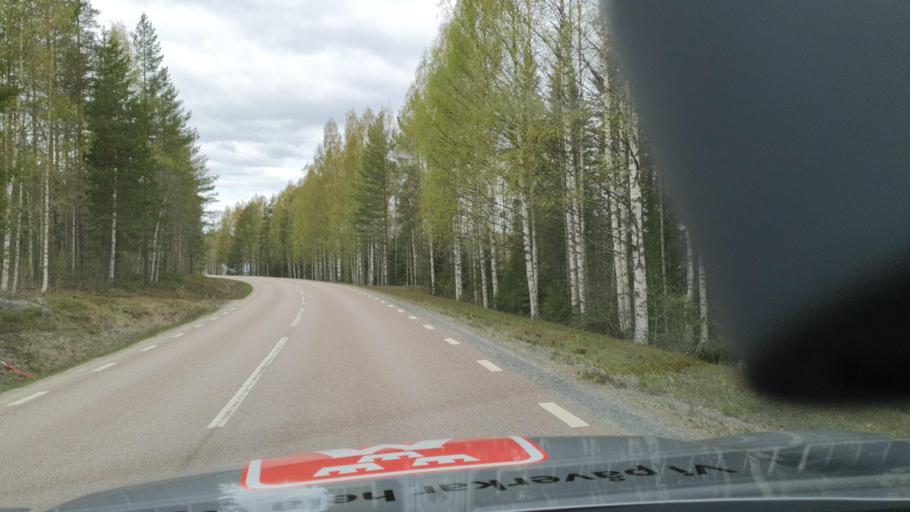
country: SE
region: Vaesternorrland
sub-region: OErnskoeldsviks Kommun
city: Ornskoldsvik
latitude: 63.4934
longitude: 18.8720
